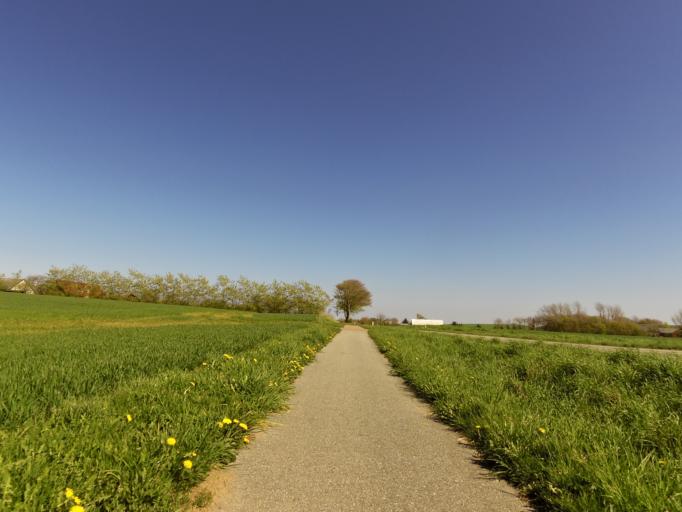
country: DK
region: Central Jutland
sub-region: Holstebro Kommune
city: Vinderup
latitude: 56.6005
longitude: 8.7469
